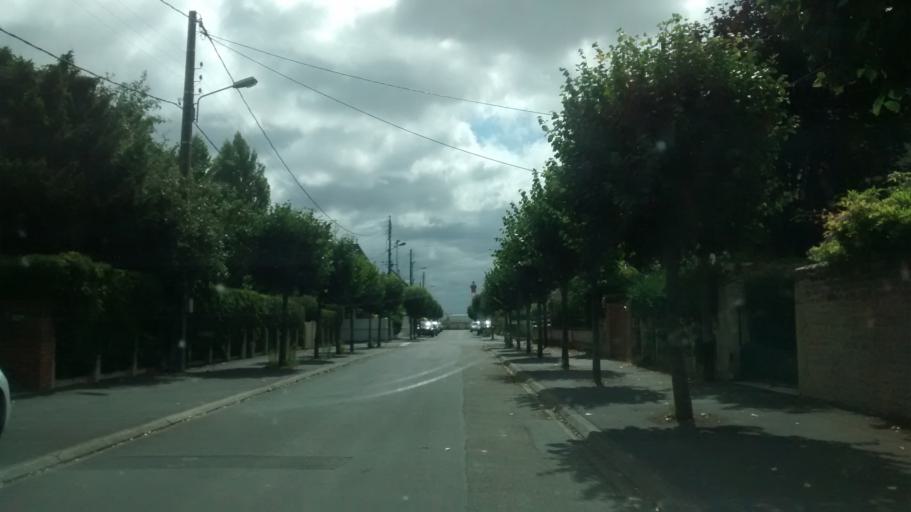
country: FR
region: Lower Normandy
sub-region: Departement du Calvados
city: Ouistreham
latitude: 49.2837
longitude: -0.2558
